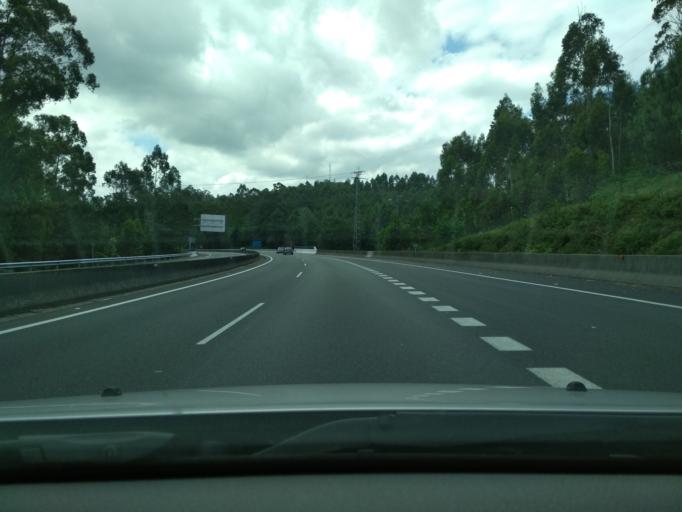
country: ES
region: Galicia
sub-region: Provincia de Pontevedra
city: Portas
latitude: 42.5955
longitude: -8.6776
